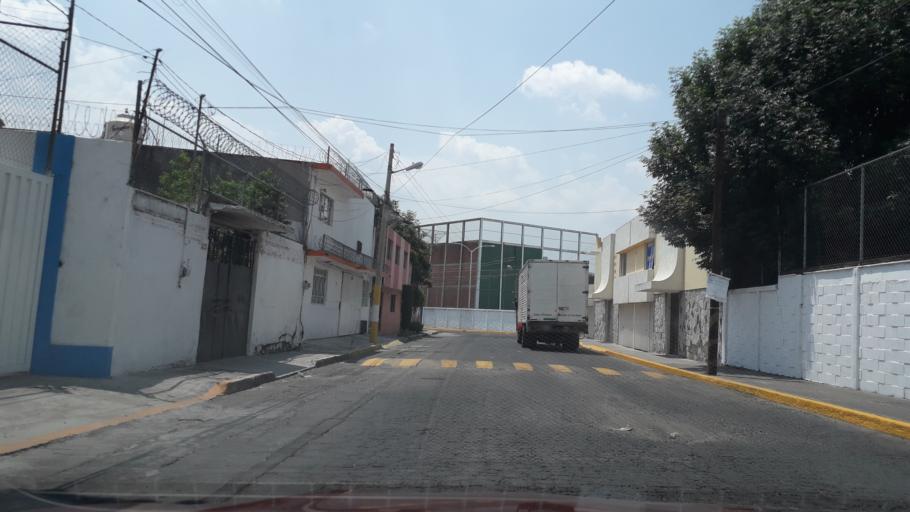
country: MX
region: Puebla
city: Puebla
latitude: 19.0470
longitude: -98.1693
